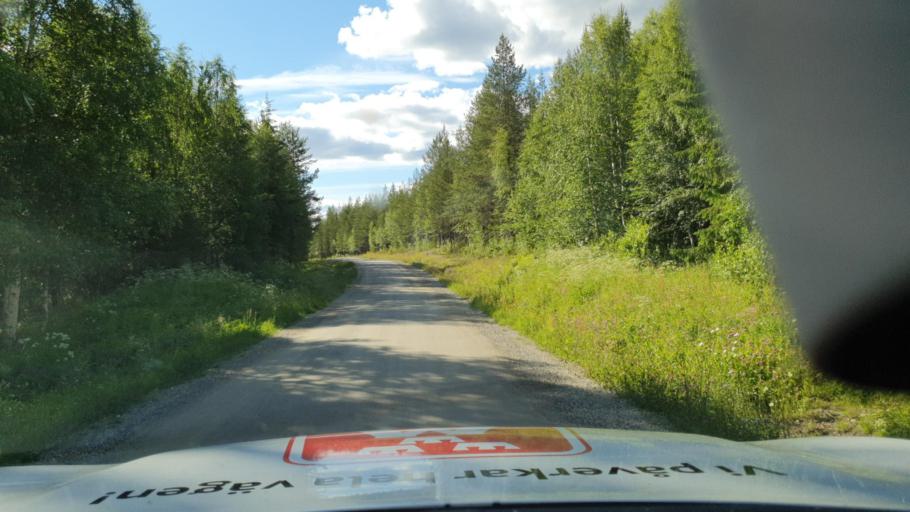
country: SE
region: Vaesterbotten
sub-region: Lycksele Kommun
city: Lycksele
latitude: 64.4094
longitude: 18.5029
